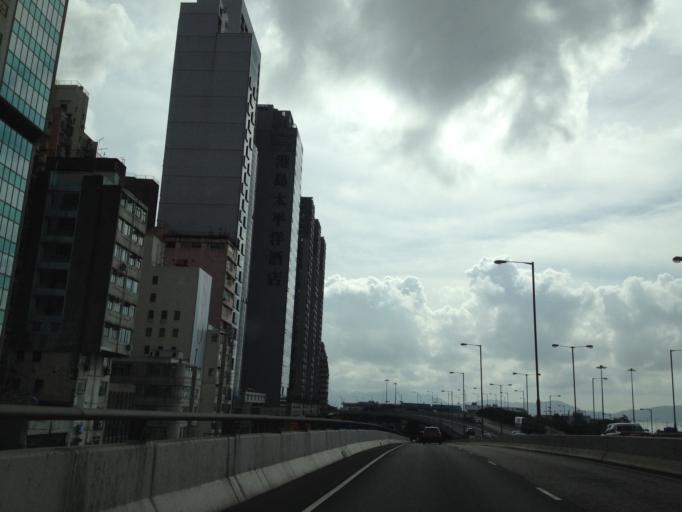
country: HK
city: Hong Kong
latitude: 22.2887
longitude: 114.1448
